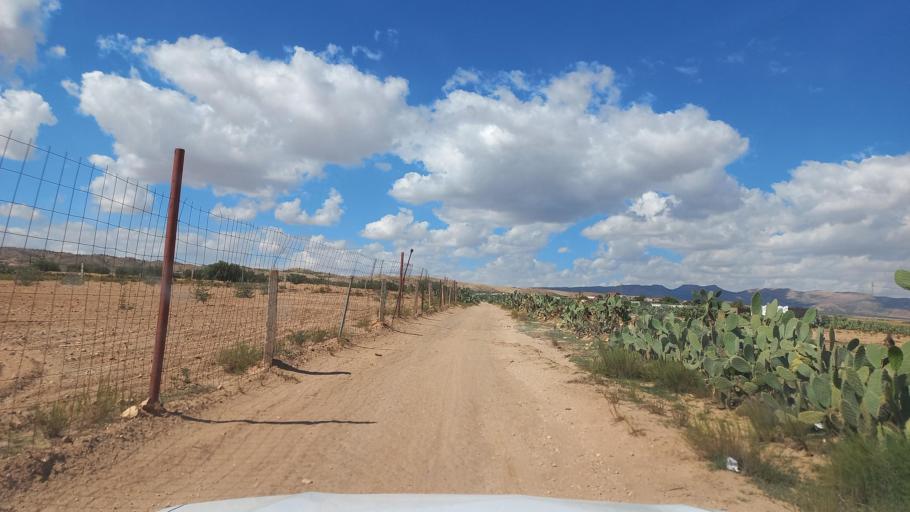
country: TN
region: Al Qasrayn
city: Sbiba
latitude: 35.3544
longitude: 9.0189
